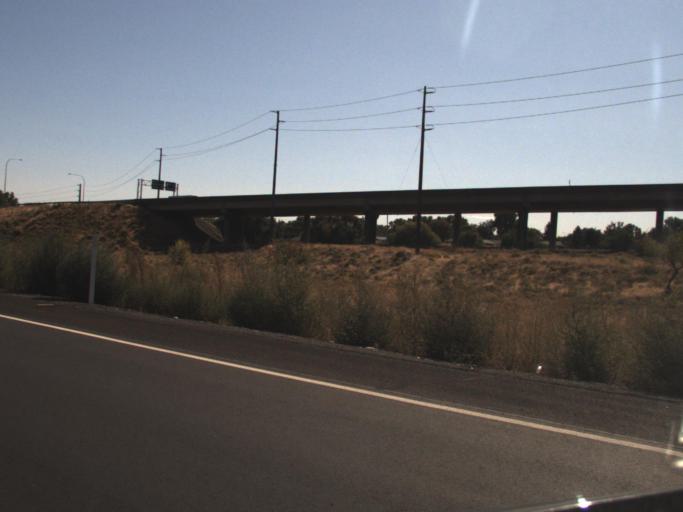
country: US
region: Washington
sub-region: Benton County
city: Kennewick
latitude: 46.2170
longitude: -119.1434
